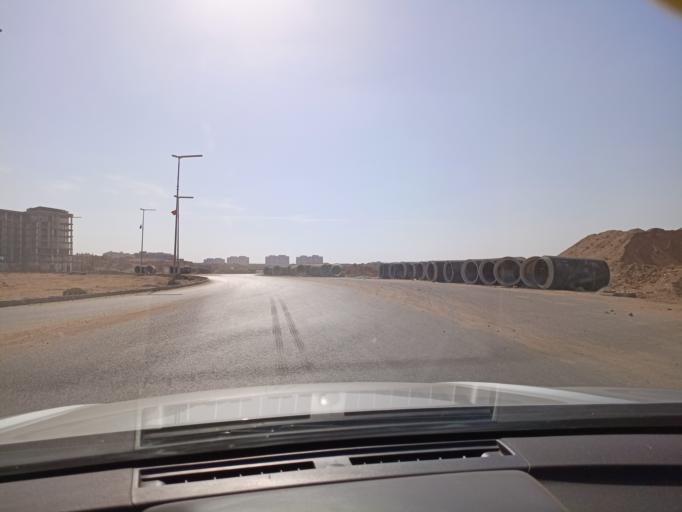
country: EG
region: Muhafazat al Qalyubiyah
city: Al Khankah
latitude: 30.0390
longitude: 31.6838
